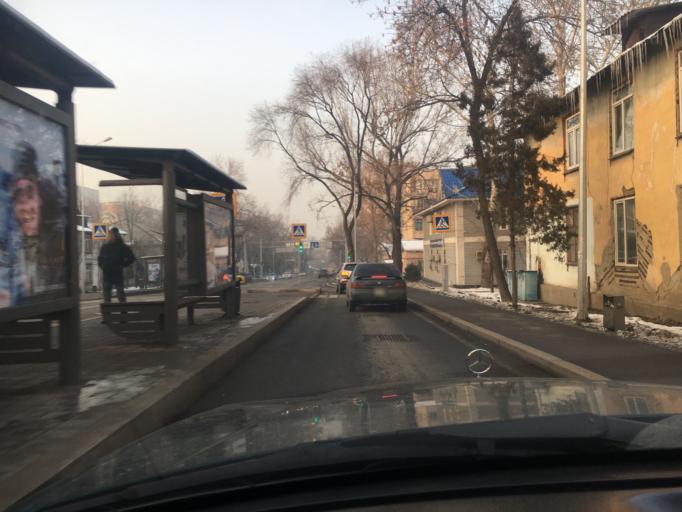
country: KZ
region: Almaty Qalasy
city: Almaty
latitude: 43.2094
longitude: 76.8787
